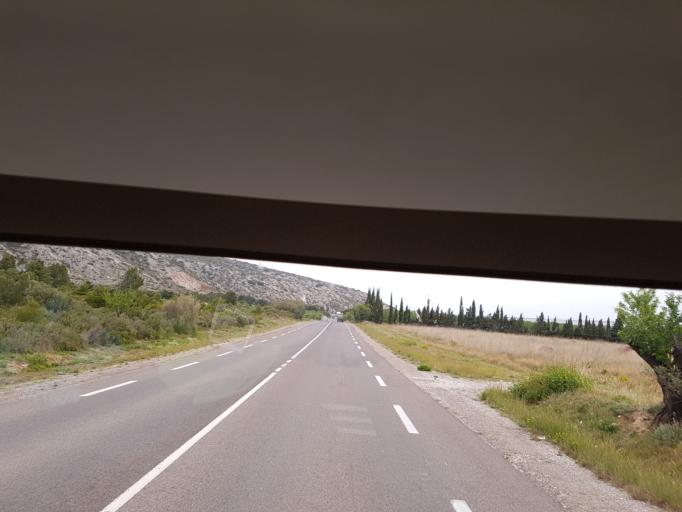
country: FR
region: Languedoc-Roussillon
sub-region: Departement des Pyrenees-Orientales
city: Salses-le-Chateau
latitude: 42.8548
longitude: 2.9482
